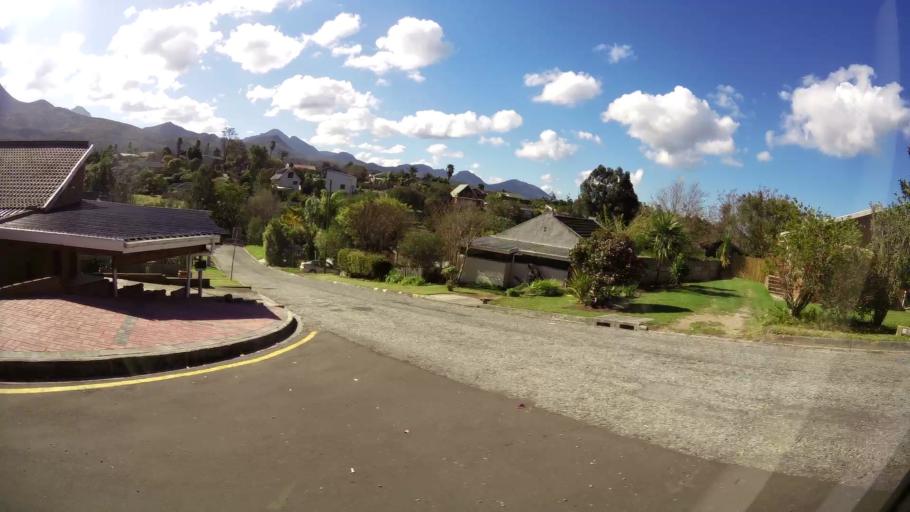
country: ZA
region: Western Cape
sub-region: Eden District Municipality
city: George
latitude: -33.9501
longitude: 22.4775
